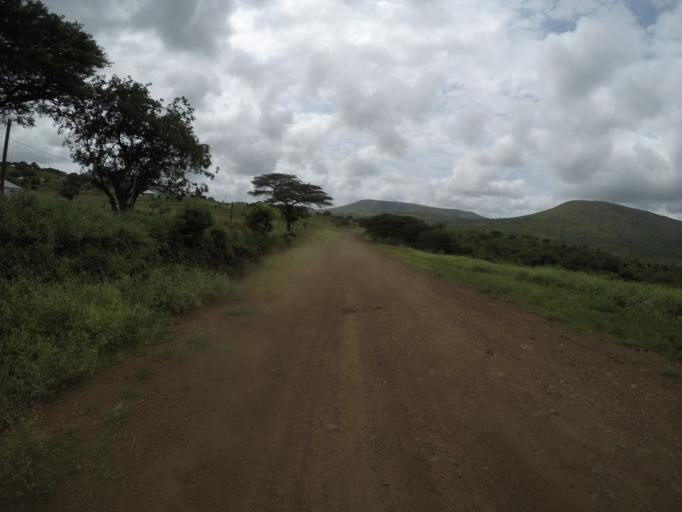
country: ZA
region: KwaZulu-Natal
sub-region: uThungulu District Municipality
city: Empangeni
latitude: -28.5919
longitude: 31.8862
